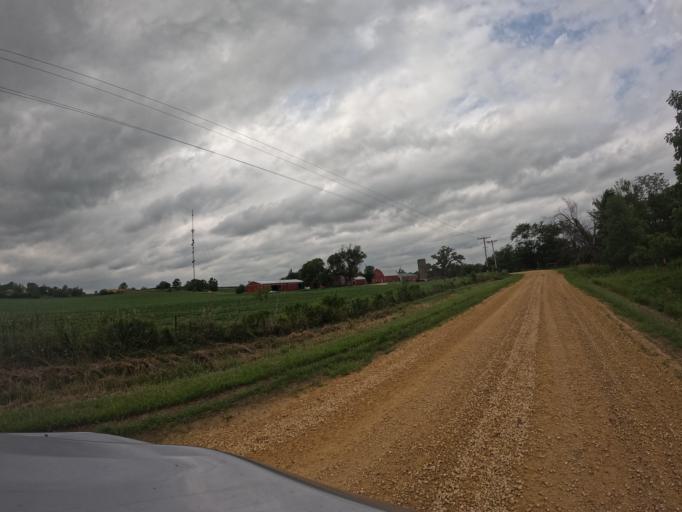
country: US
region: Iowa
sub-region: Clinton County
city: De Witt
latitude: 41.8026
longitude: -90.5682
